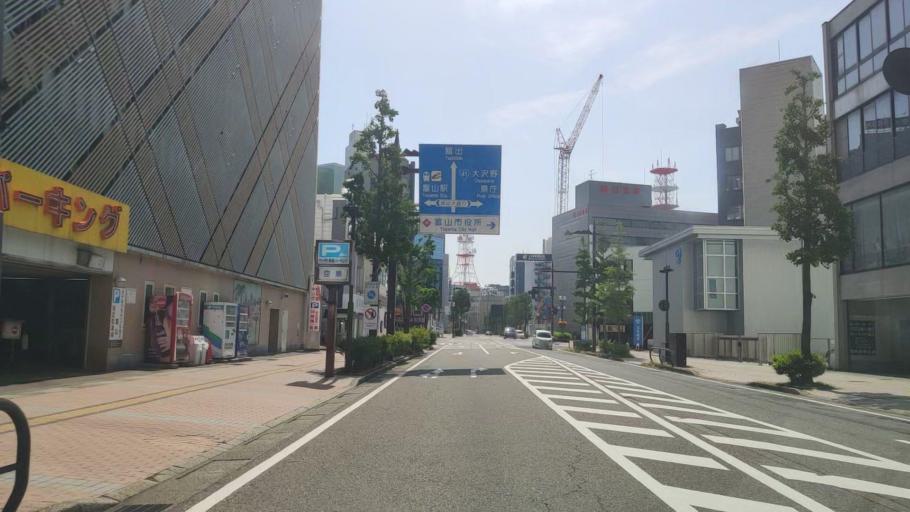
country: JP
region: Toyama
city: Toyama-shi
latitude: 36.6983
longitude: 137.2123
